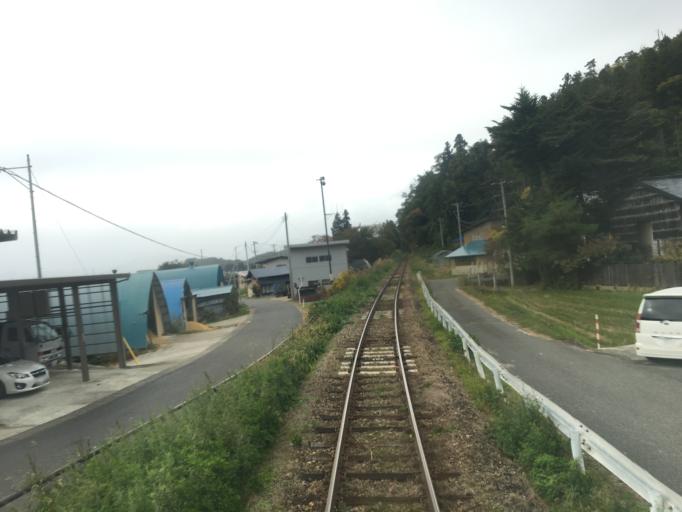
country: JP
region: Yamagata
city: Nagai
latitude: 38.0524
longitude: 140.0771
